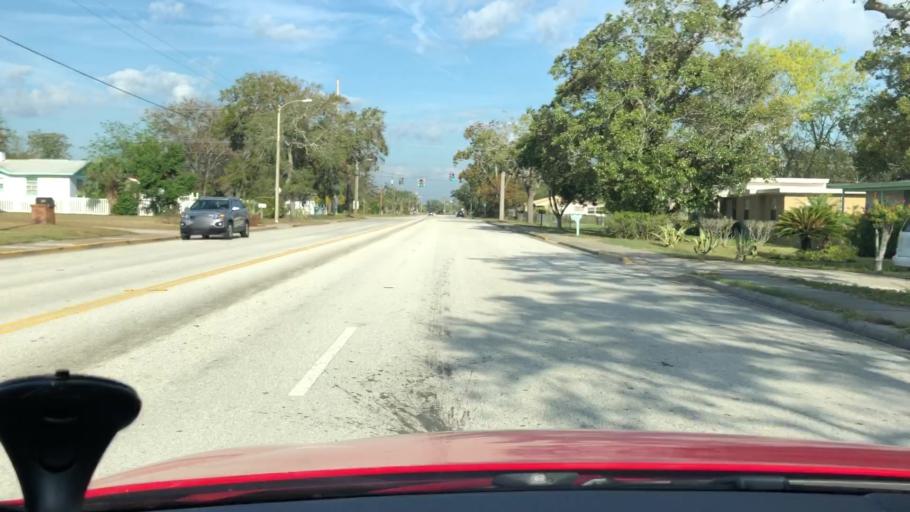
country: US
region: Florida
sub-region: Volusia County
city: Daytona Beach
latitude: 29.2133
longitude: -81.0521
